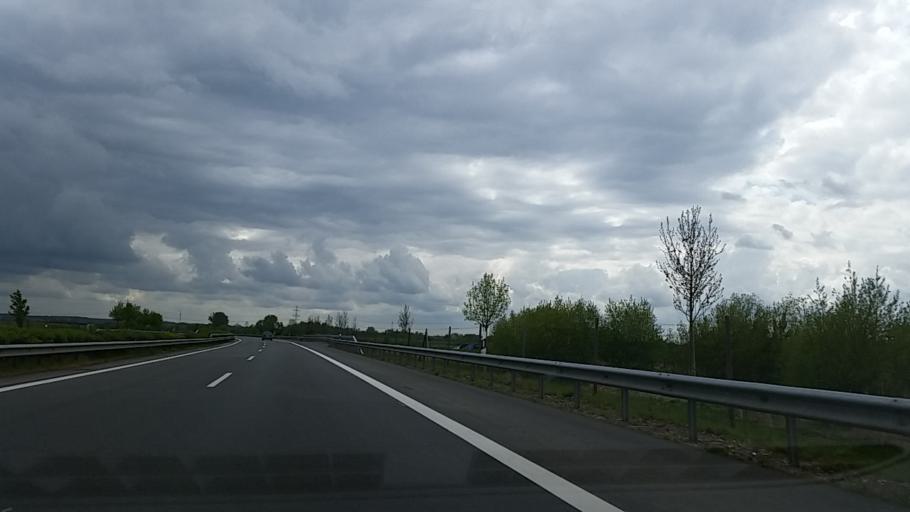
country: DE
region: Lower Saxony
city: Horneburg
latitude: 53.5304
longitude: 9.5792
